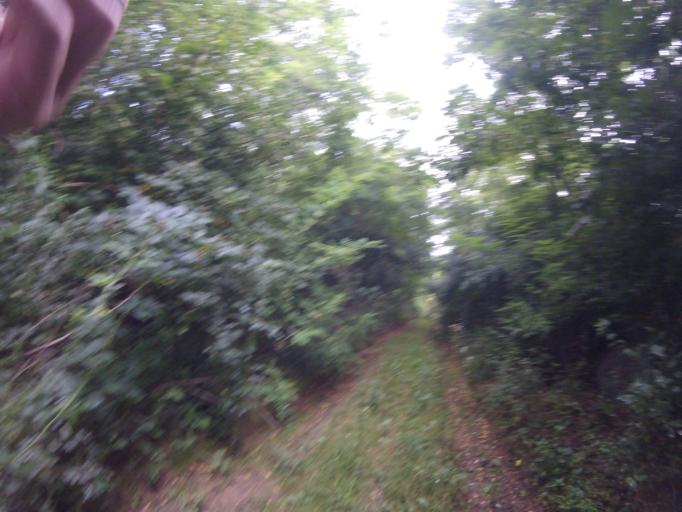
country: SK
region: Nitriansky
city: Sahy
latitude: 48.0466
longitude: 18.9245
